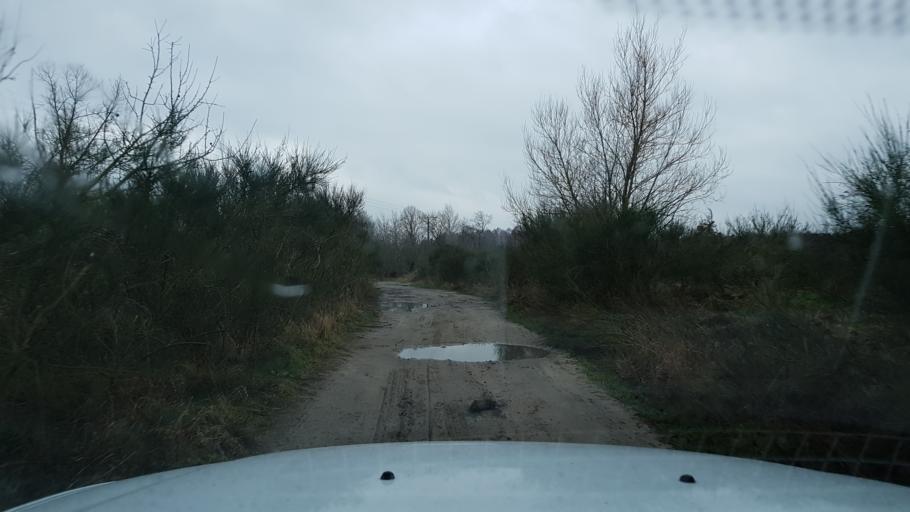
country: PL
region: West Pomeranian Voivodeship
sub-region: Powiat gryficki
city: Brojce
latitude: 53.9786
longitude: 15.3048
